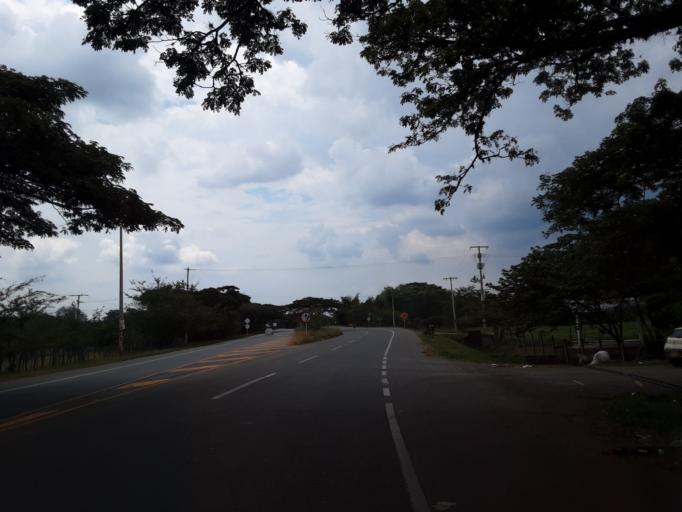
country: CO
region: Cauca
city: Santander de Quilichao
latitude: 3.0245
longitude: -76.4817
